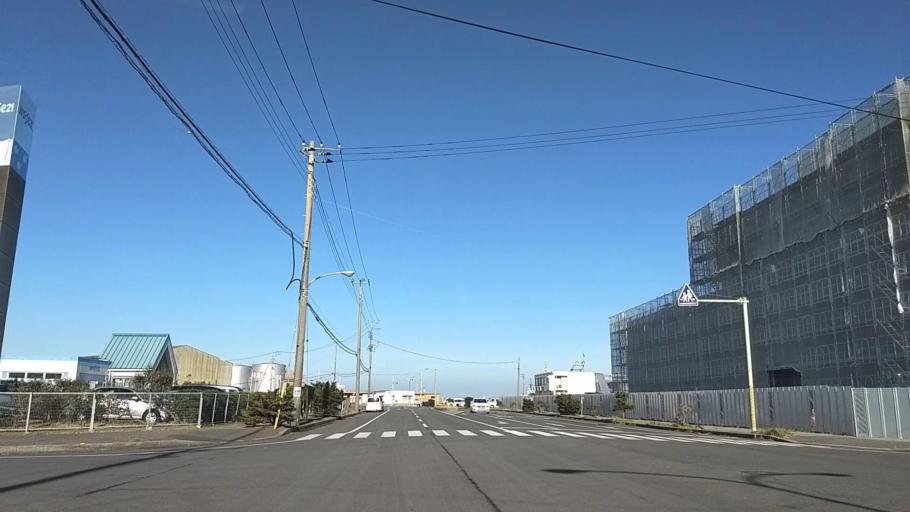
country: JP
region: Chiba
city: Hasaki
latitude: 35.7404
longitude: 140.8649
